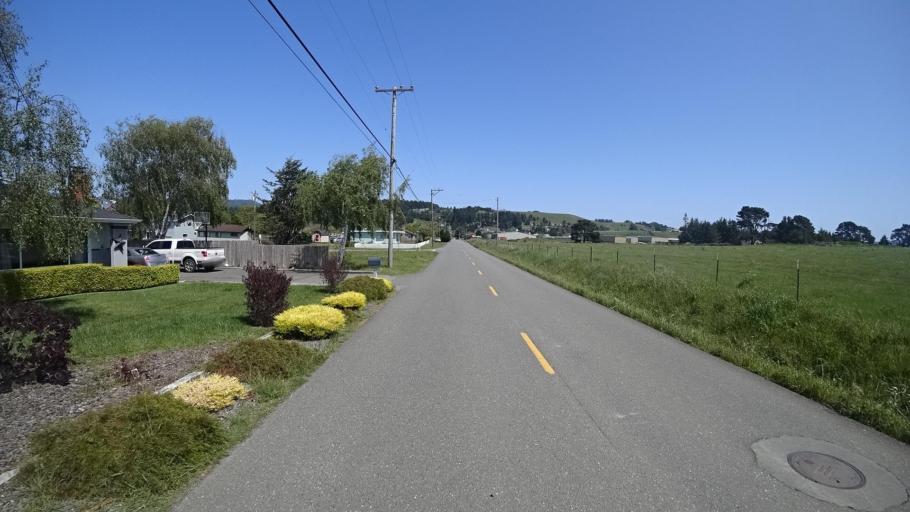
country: US
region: California
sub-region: Humboldt County
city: Hydesville
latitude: 40.5630
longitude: -124.1356
